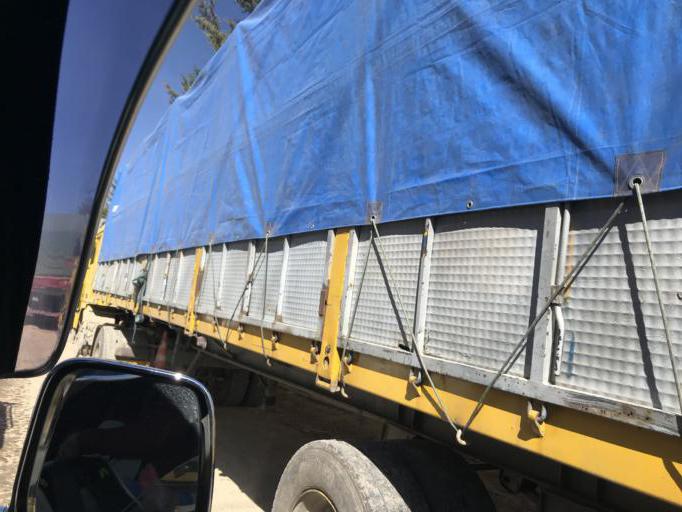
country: BO
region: La Paz
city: La Paz
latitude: -16.4872
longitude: -68.2109
